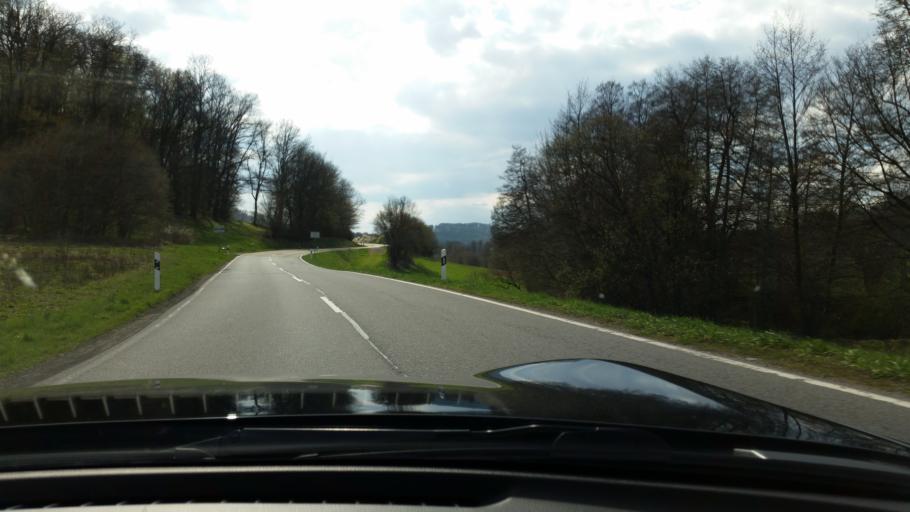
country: DE
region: Baden-Wuerttemberg
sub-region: Regierungsbezirk Stuttgart
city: Roigheim
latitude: 49.3679
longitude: 9.3596
